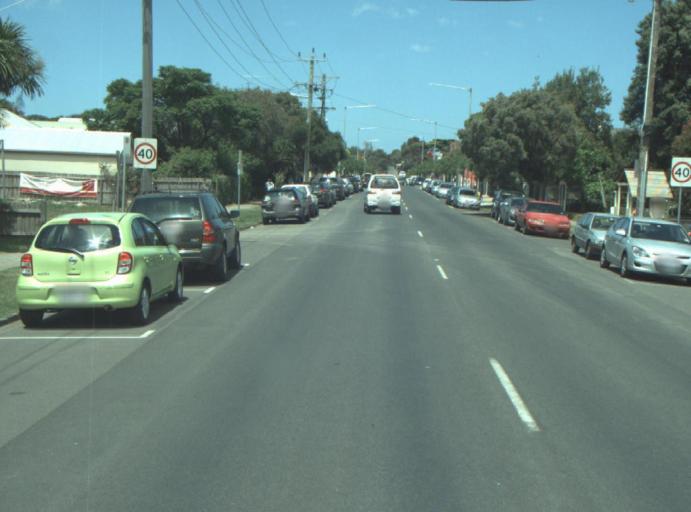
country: AU
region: Victoria
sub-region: Greater Geelong
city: Leopold
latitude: -38.2797
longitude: 144.4920
